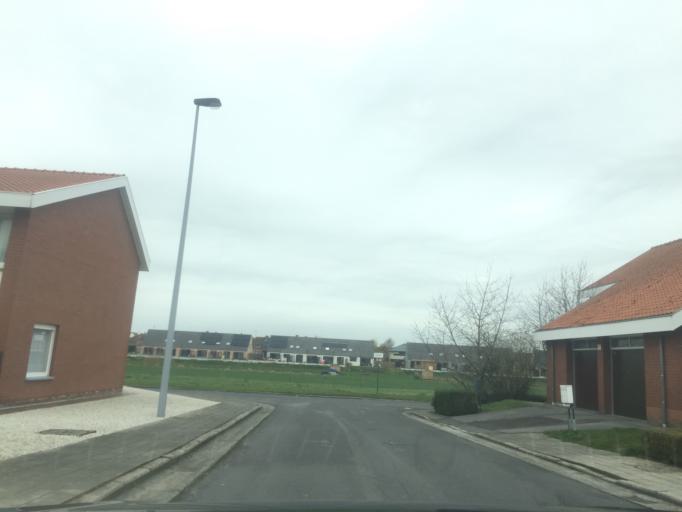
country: BE
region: Flanders
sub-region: Provincie West-Vlaanderen
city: Meulebeke
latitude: 50.9408
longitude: 3.2927
